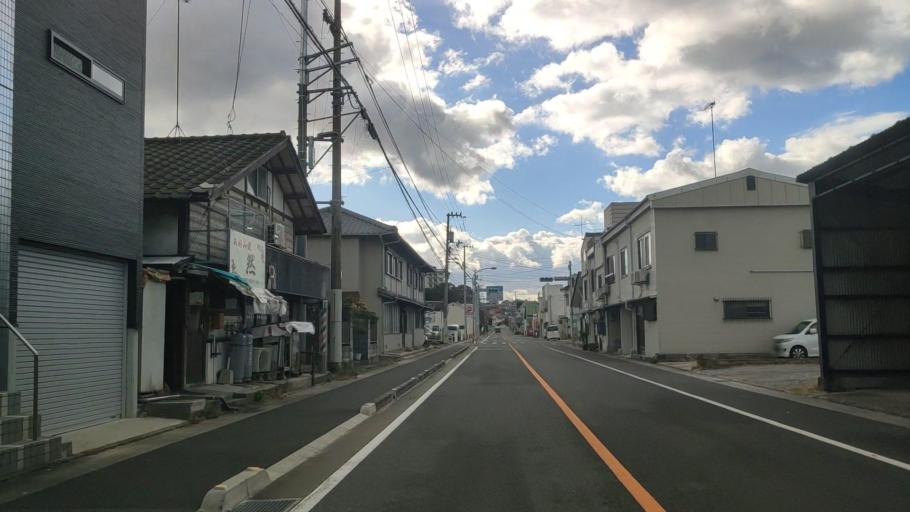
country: JP
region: Ehime
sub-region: Shikoku-chuo Shi
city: Matsuyama
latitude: 33.8840
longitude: 132.7017
